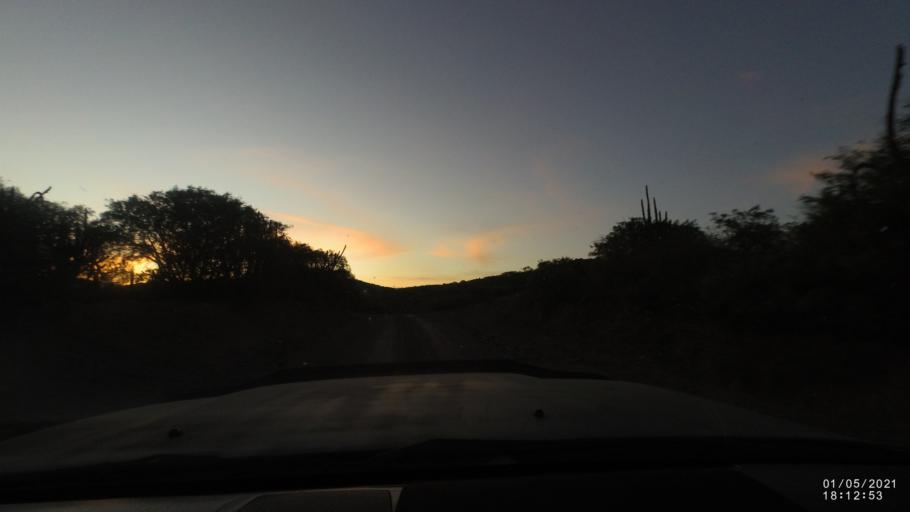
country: BO
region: Cochabamba
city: Capinota
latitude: -17.6765
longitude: -66.2035
